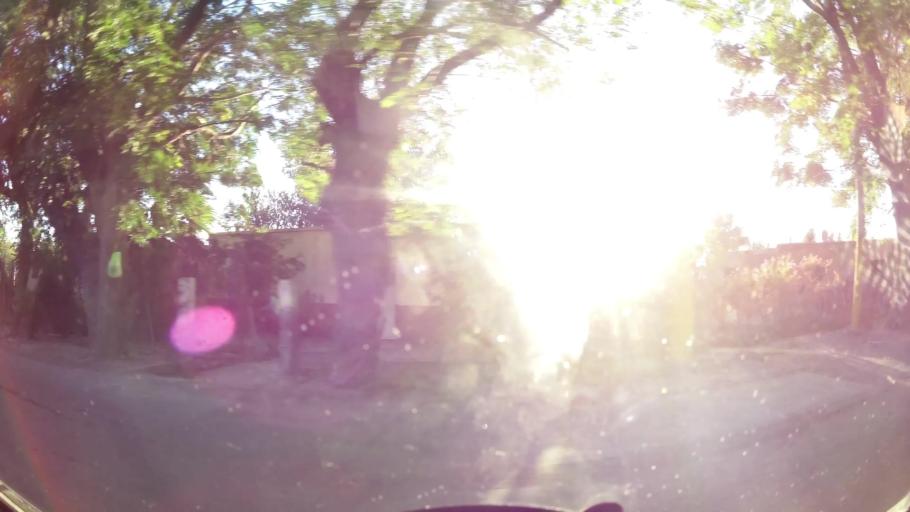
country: AR
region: San Juan
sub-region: Departamento de Santa Lucia
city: Santa Lucia
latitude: -31.5506
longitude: -68.4766
